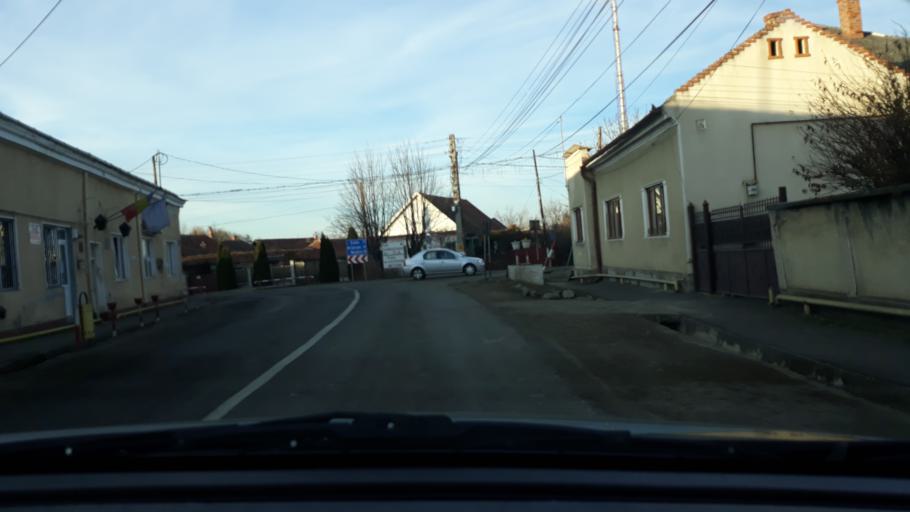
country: RO
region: Bihor
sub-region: Comuna Suplacu de Barcau
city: Suplacu de Barcau
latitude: 47.2569
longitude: 22.5316
